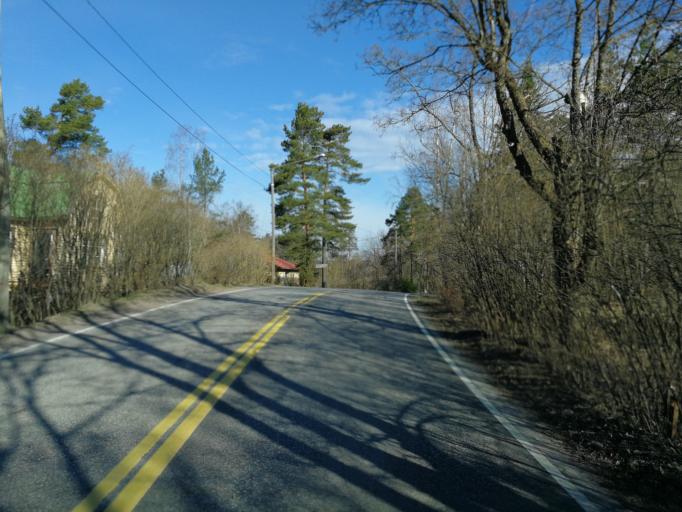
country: FI
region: Uusimaa
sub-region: Helsinki
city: Kirkkonummi
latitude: 60.2177
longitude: 24.4756
